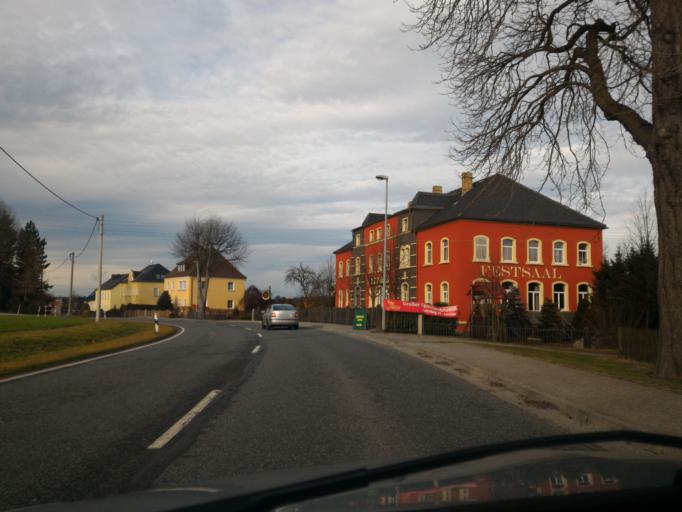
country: DE
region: Saxony
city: Demitz-Thumitz
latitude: 51.1028
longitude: 14.2195
